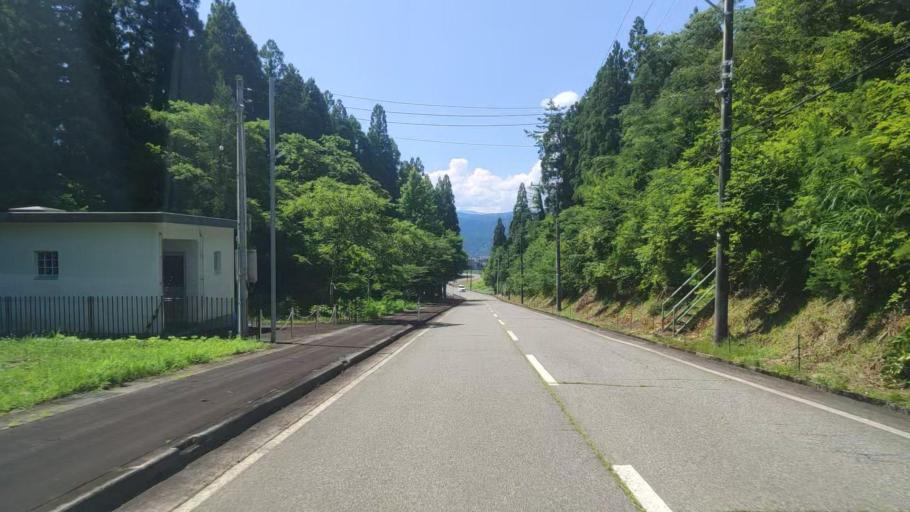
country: JP
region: Fukui
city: Katsuyama
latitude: 36.0959
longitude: 136.4909
